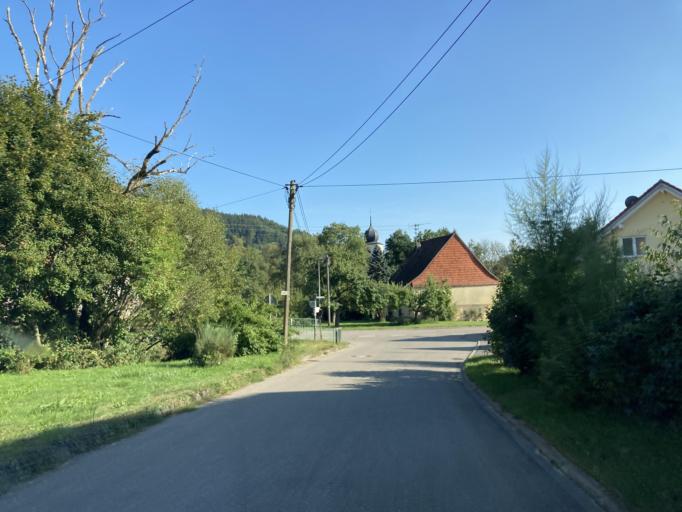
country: DE
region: Baden-Wuerttemberg
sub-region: Freiburg Region
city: Blumberg
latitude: 47.8383
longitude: 8.5017
